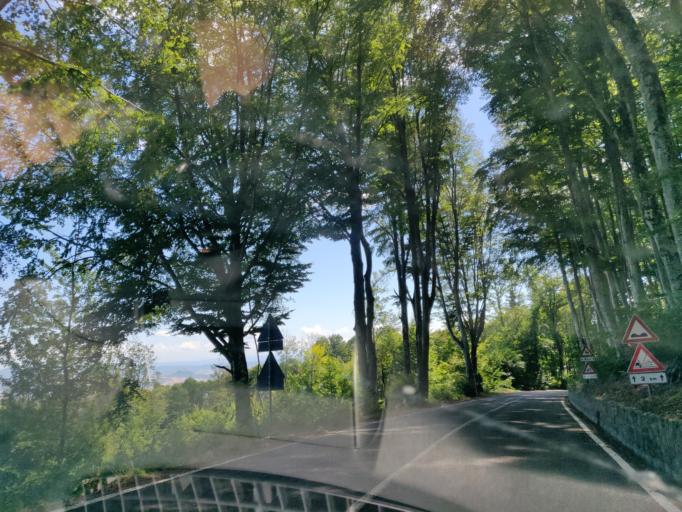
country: IT
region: Tuscany
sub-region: Provincia di Siena
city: Abbadia San Salvatore
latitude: 42.9011
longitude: 11.6453
